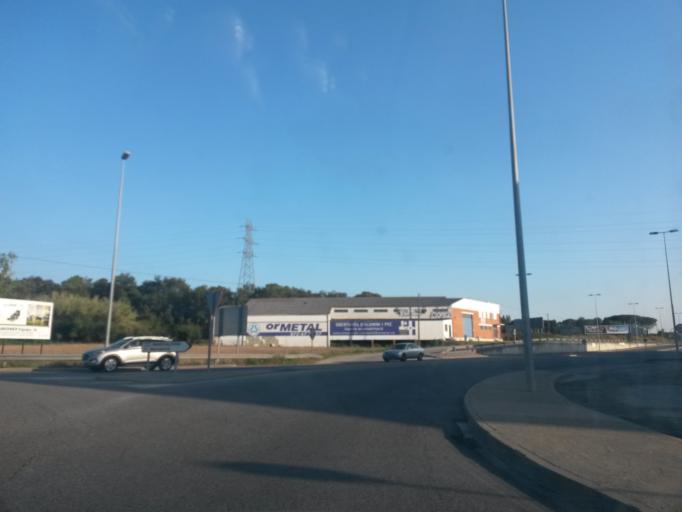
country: ES
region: Catalonia
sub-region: Provincia de Girona
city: Fornells de la Selva
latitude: 41.9407
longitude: 2.8025
